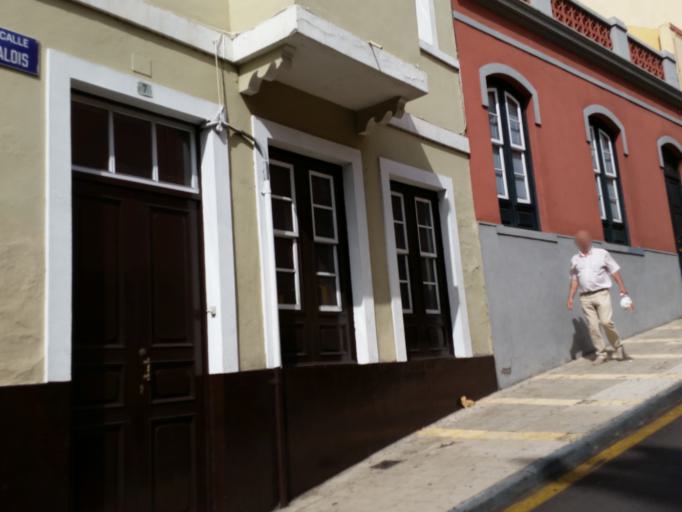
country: ES
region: Canary Islands
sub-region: Provincia de Santa Cruz de Tenerife
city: Puerto de la Cruz
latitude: 28.4149
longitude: -16.5492
